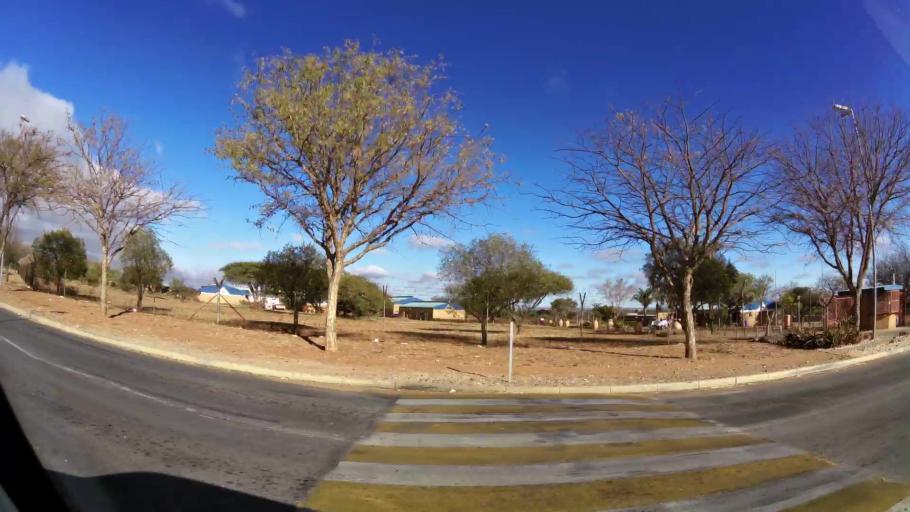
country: ZA
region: Limpopo
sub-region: Capricorn District Municipality
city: Polokwane
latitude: -23.9194
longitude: 29.4765
